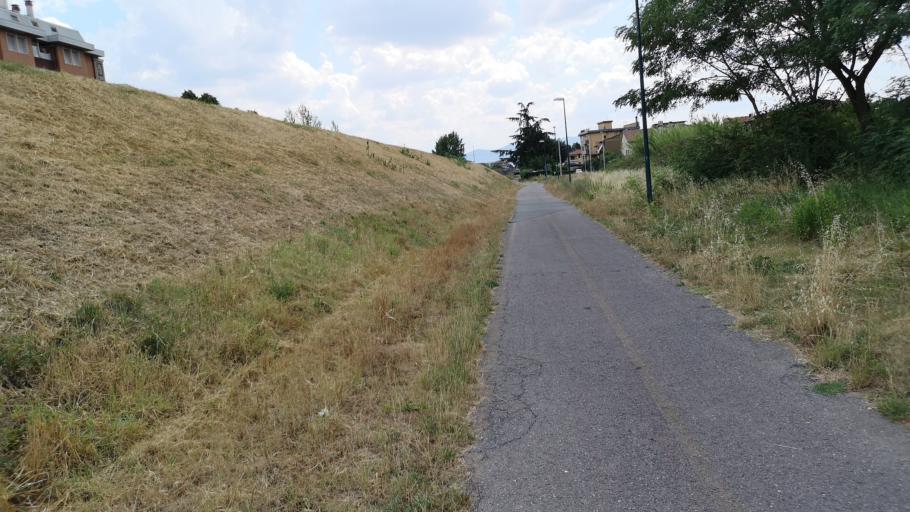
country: IT
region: Tuscany
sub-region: Provincia di Prato
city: Fornacelle
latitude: 43.8984
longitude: 11.0628
